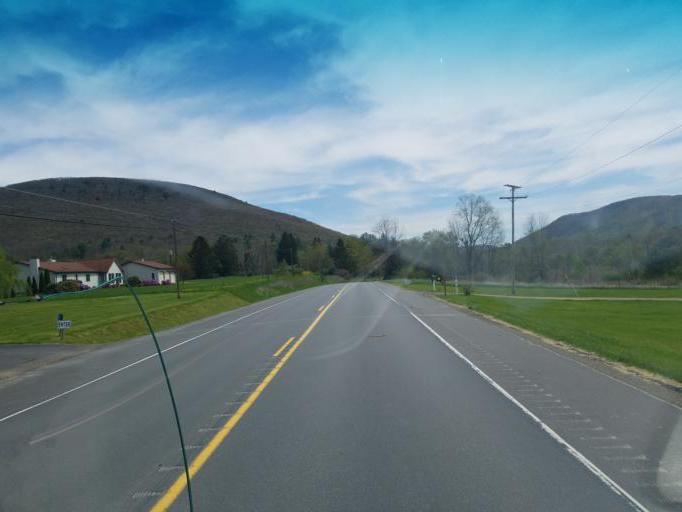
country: US
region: Pennsylvania
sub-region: Potter County
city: Galeton
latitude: 41.7451
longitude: -77.6018
